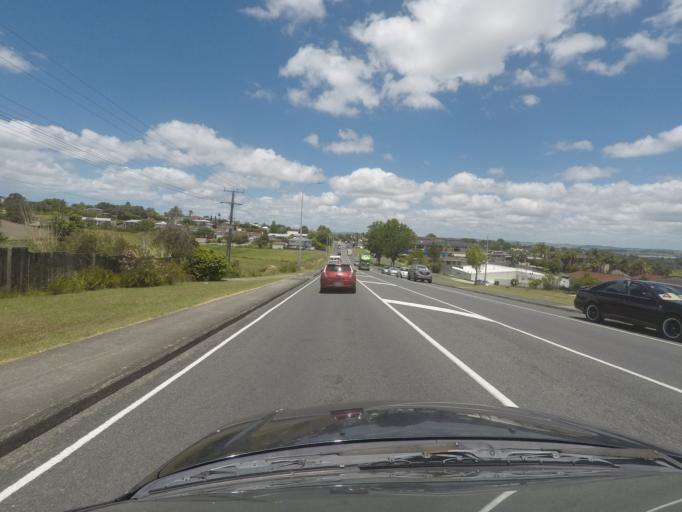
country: NZ
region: Northland
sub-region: Whangarei
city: Whangarei
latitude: -35.7523
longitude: 174.3681
